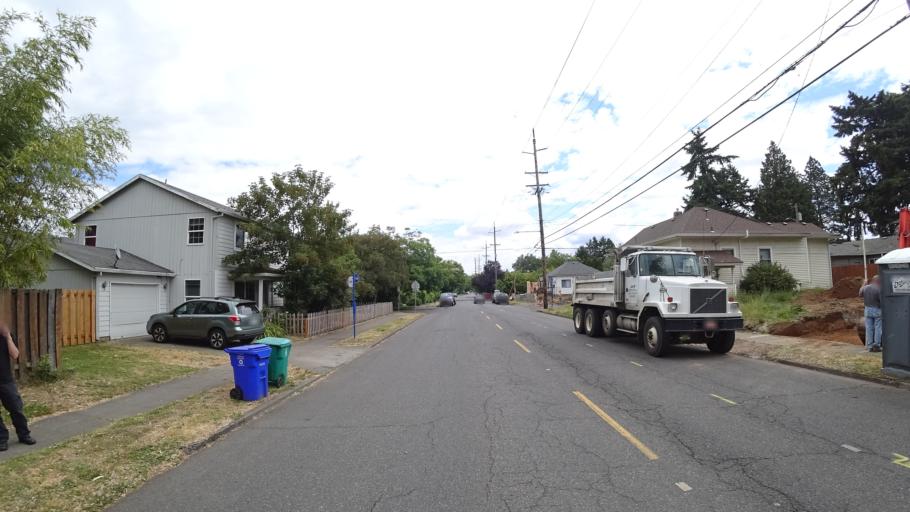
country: US
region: Oregon
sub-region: Multnomah County
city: Portland
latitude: 45.5841
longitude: -122.7180
